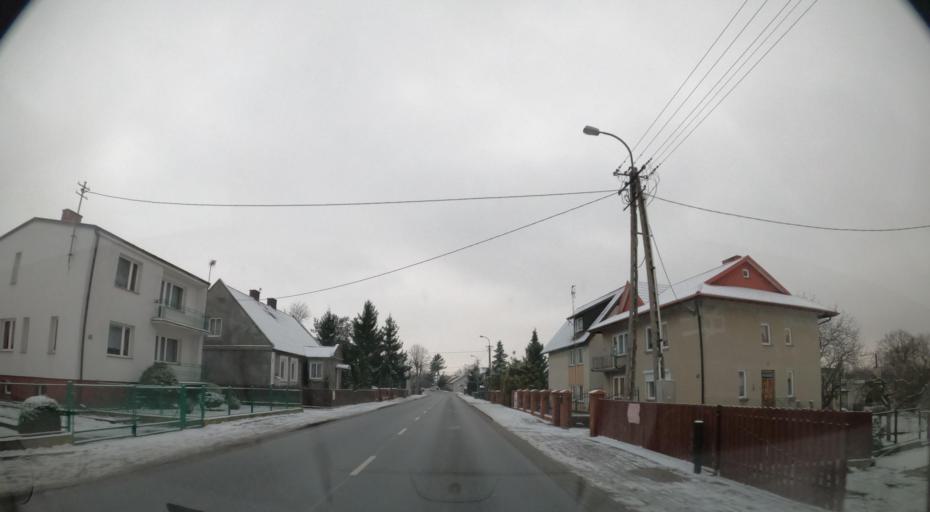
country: PL
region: Kujawsko-Pomorskie
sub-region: Powiat lipnowski
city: Wielgie
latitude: 52.7404
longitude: 19.2664
